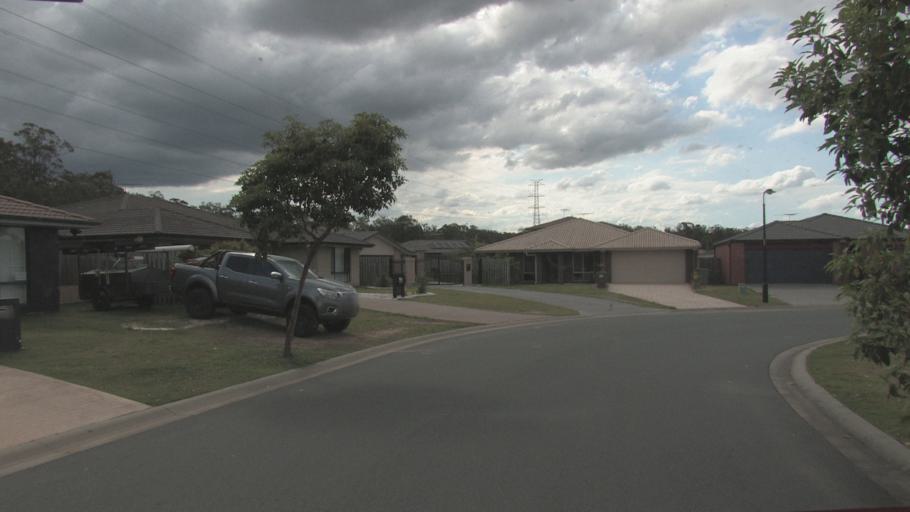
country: AU
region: Queensland
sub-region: Logan
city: Woodridge
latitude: -27.6602
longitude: 153.0764
